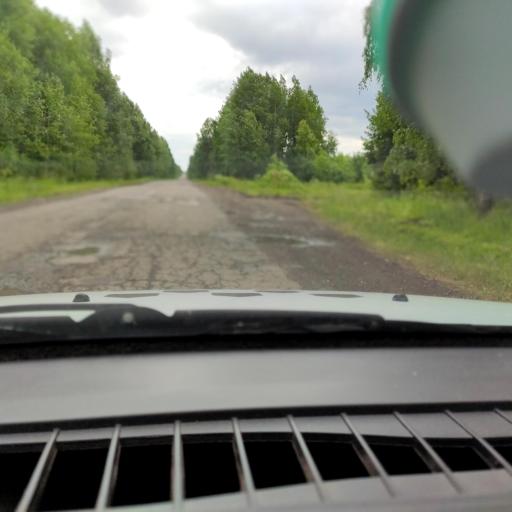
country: RU
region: Perm
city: Kukushtan
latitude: 57.2810
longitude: 56.5355
